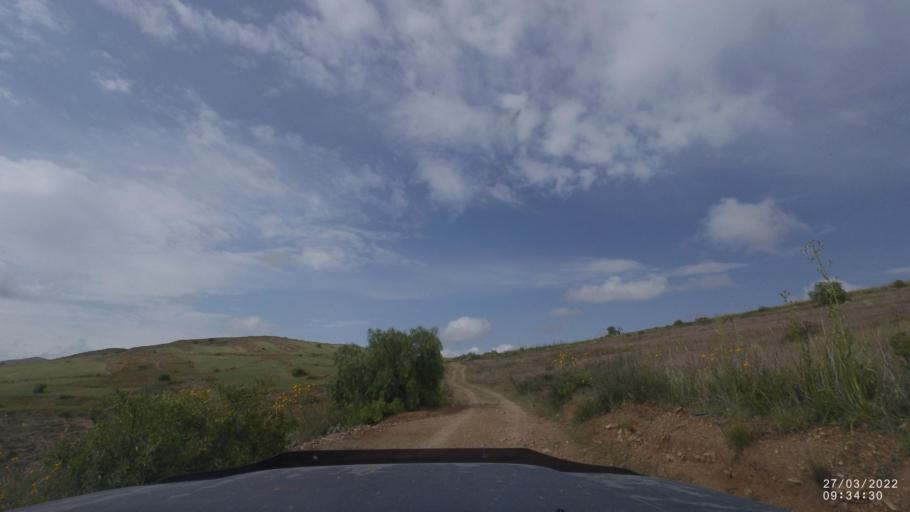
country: BO
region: Cochabamba
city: Cliza
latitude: -17.7427
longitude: -65.8910
